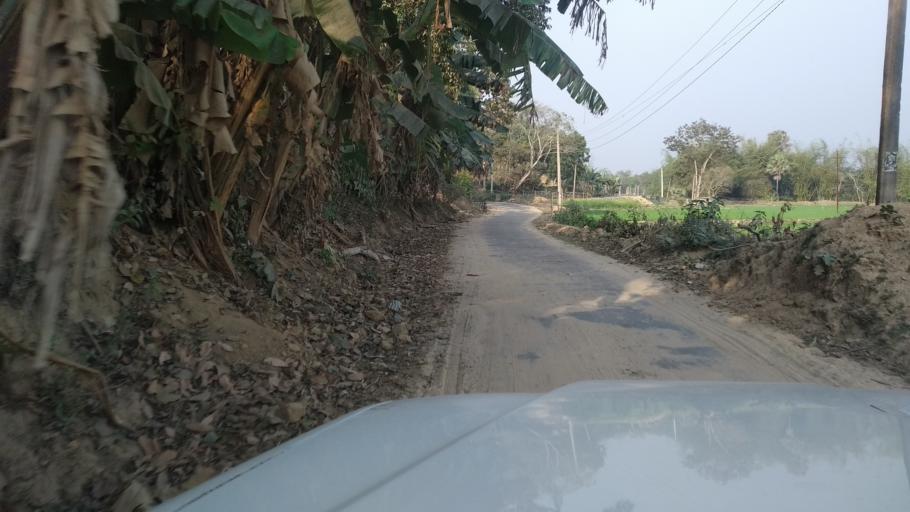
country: IN
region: Tripura
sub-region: West Tripura
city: Sonamura
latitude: 23.4263
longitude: 91.3005
